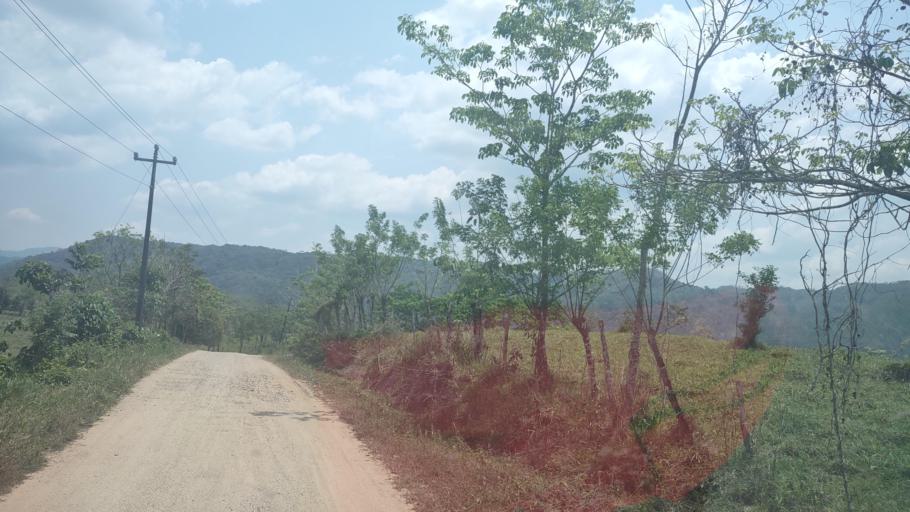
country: MX
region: Chiapas
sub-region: Tecpatan
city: Raudales Malpaso
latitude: 17.2798
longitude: -93.8699
